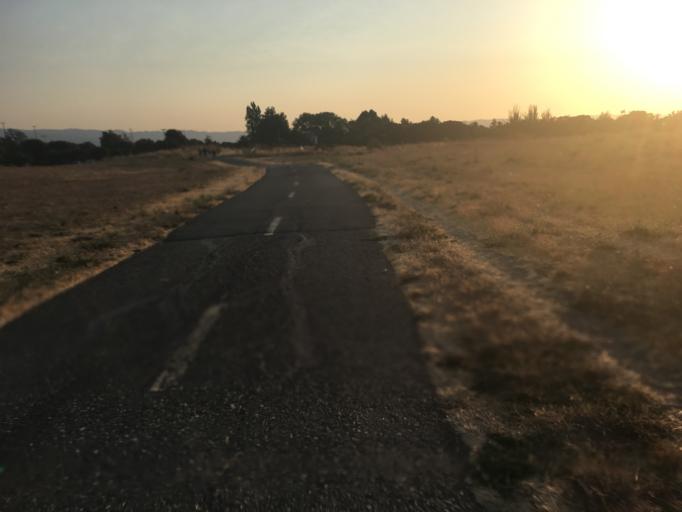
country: US
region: California
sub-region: Santa Clara County
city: Mountain View
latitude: 37.4326
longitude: -122.0840
